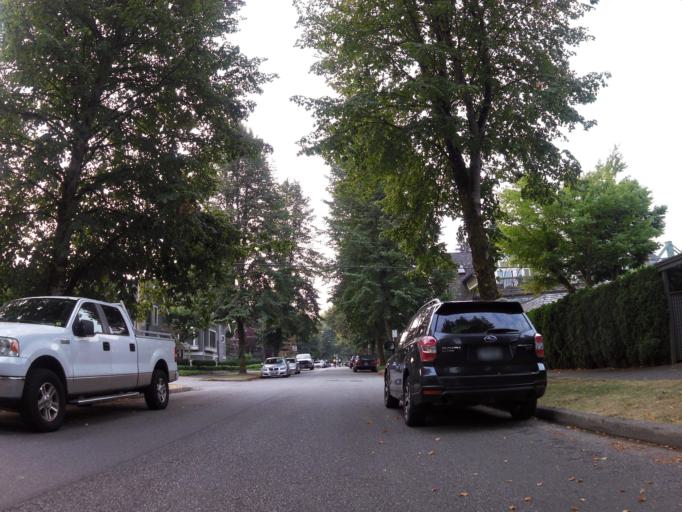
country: CA
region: British Columbia
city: West End
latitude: 49.2588
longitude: -123.1483
